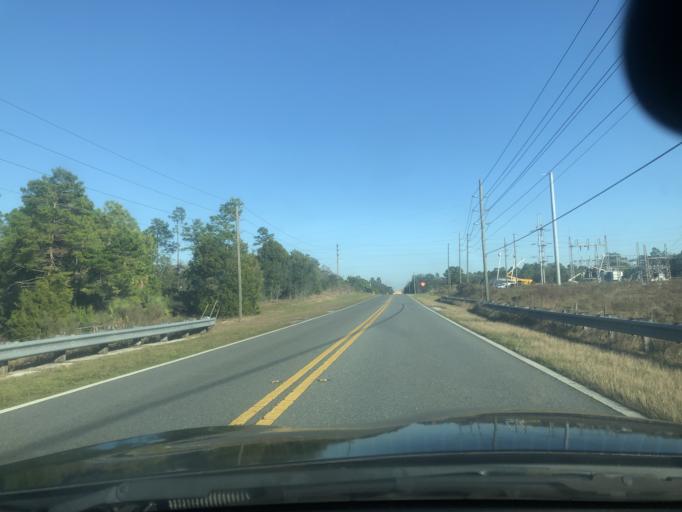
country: US
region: Florida
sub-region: Citrus County
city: Sugarmill Woods
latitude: 28.7640
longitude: -82.5193
